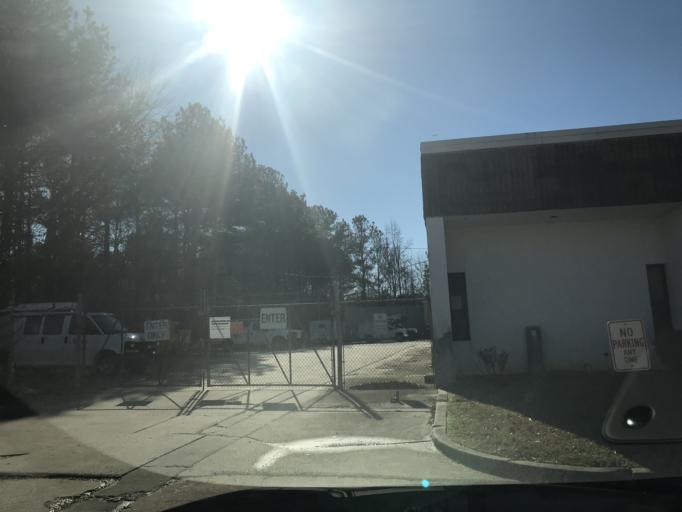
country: US
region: Georgia
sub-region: Clayton County
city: Morrow
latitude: 33.5696
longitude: -84.3576
